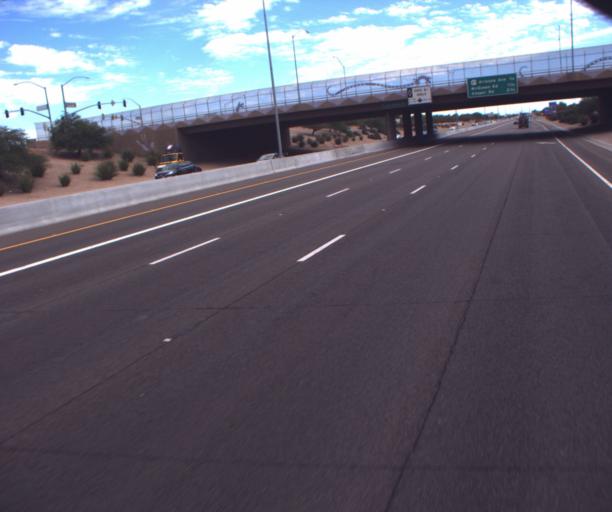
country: US
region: Arizona
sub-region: Maricopa County
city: Chandler
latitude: 33.2871
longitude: -111.8600
